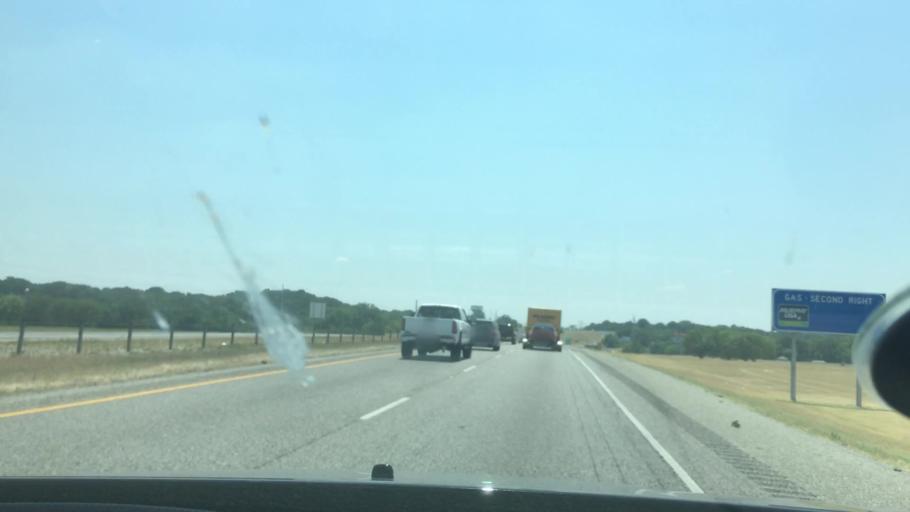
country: US
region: Oklahoma
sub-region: Bryan County
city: Durant
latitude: 34.0218
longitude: -96.3890
